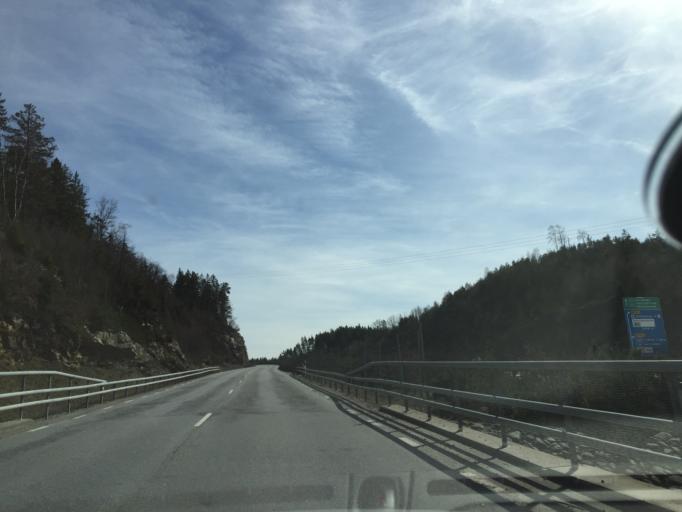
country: SE
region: Vaestra Goetaland
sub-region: Uddevalla Kommun
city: Uddevalla
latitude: 58.3694
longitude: 11.7938
